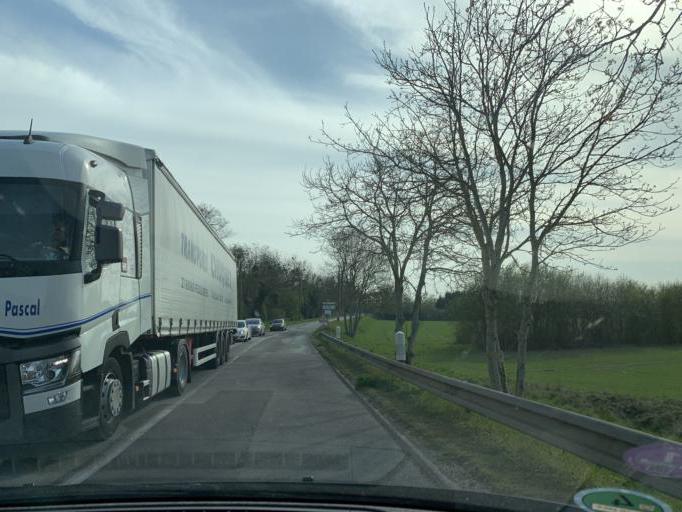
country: FR
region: Haute-Normandie
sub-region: Departement de l'Eure
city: Les Andelys
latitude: 49.2361
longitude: 1.3966
